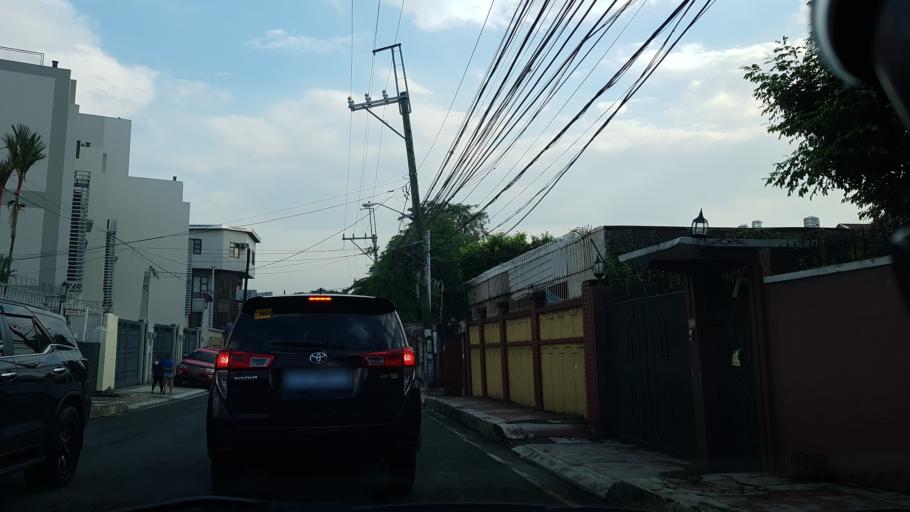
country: PH
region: Metro Manila
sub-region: Quezon City
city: Quezon City
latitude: 14.6385
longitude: 121.0581
